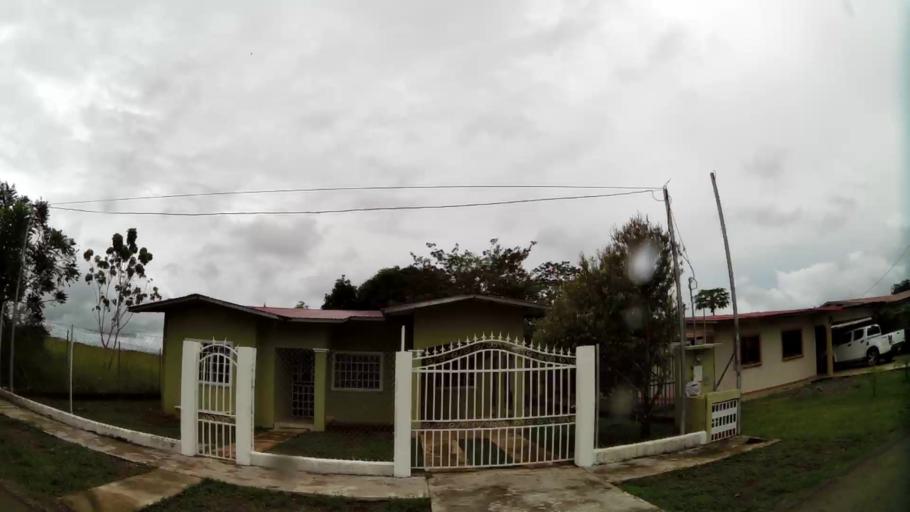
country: PA
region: Chiriqui
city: David
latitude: 8.4002
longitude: -82.4538
